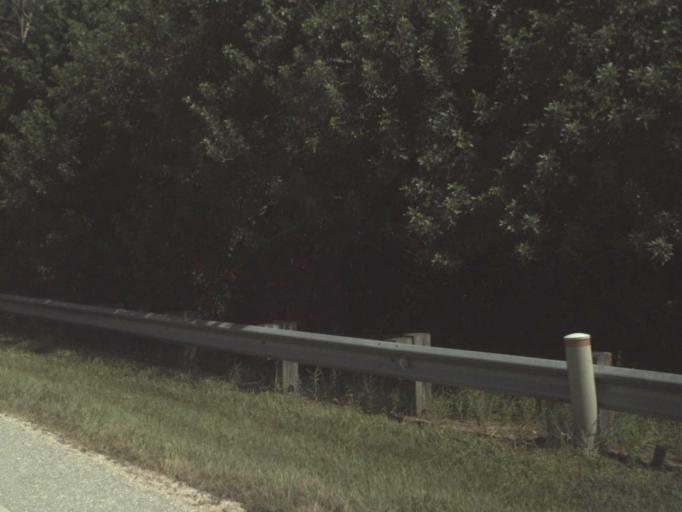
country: US
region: Florida
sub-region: Okeechobee County
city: Taylor Creek
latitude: 27.1350
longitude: -80.6411
